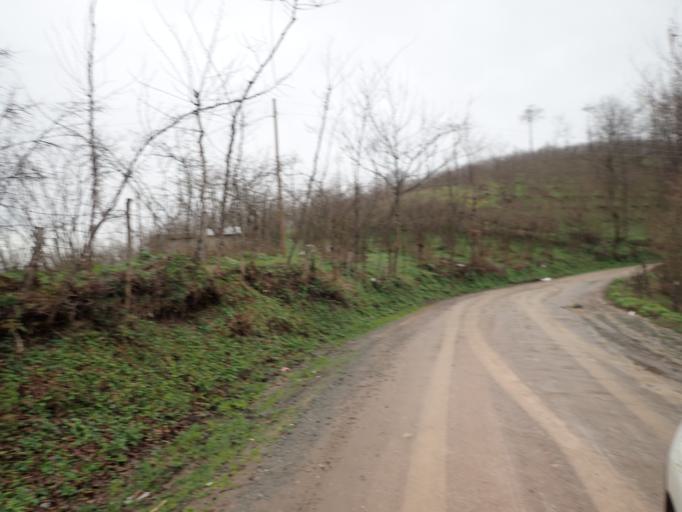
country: TR
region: Ordu
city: Camas
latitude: 40.8811
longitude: 37.4992
